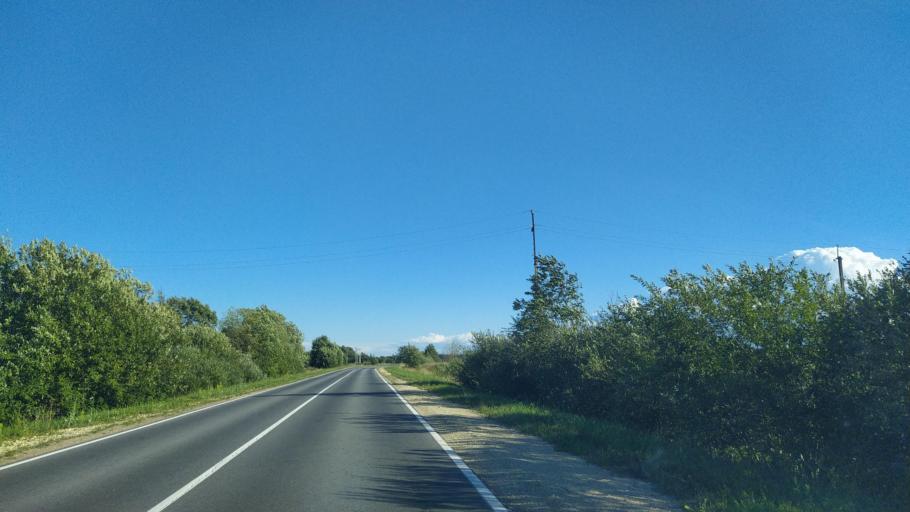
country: RU
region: Leningrad
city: Siverskiy
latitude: 59.3280
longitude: 30.0338
